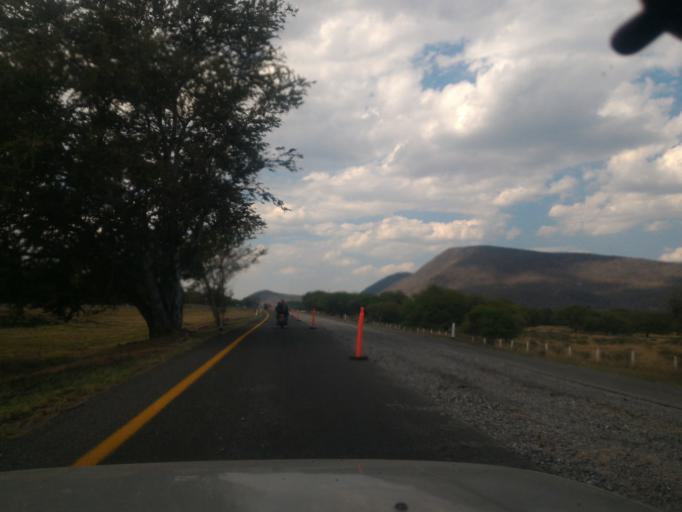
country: MX
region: Jalisco
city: Zacoalco de Torres
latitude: 20.1671
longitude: -103.5041
